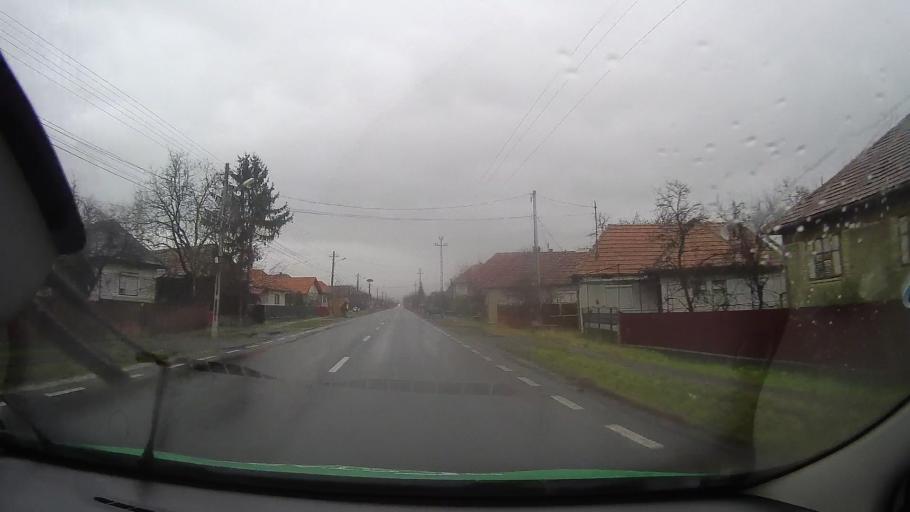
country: RO
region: Mures
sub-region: Comuna Alunis
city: Alunis
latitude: 46.8970
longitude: 24.8047
